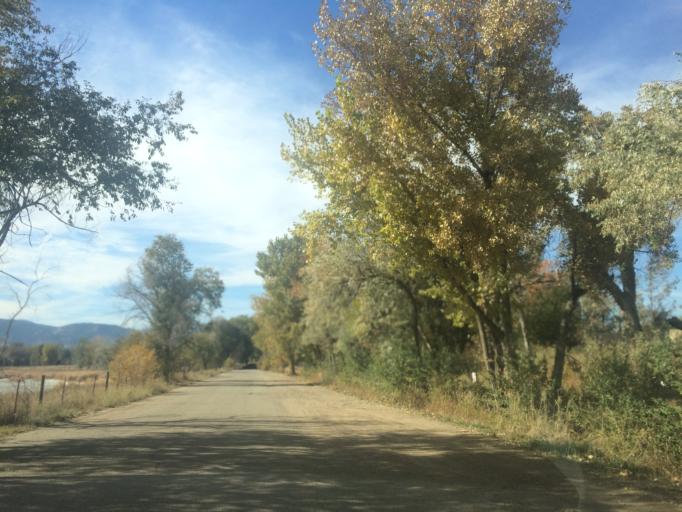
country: US
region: Colorado
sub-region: Boulder County
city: Gunbarrel
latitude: 40.0125
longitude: -105.2046
